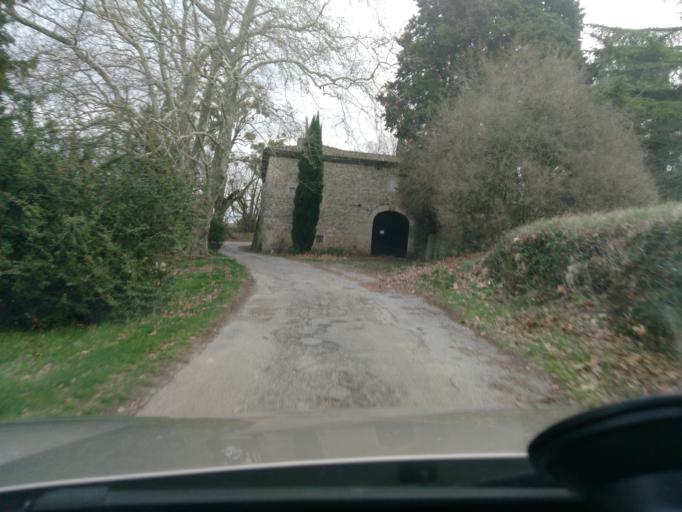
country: FR
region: Rhone-Alpes
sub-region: Departement de la Drome
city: Montboucher-sur-Jabron
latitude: 44.5390
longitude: 4.8532
